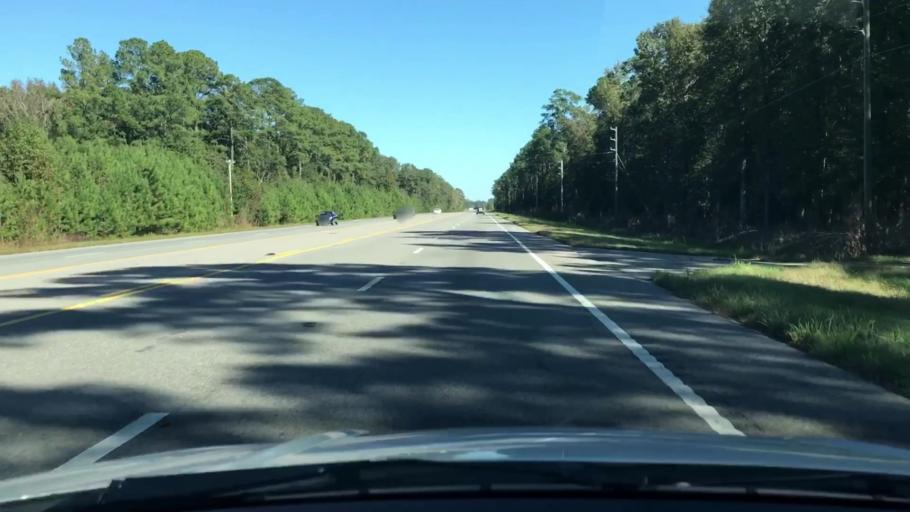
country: US
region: South Carolina
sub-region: Colleton County
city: Walterboro
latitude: 32.7698
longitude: -80.4826
